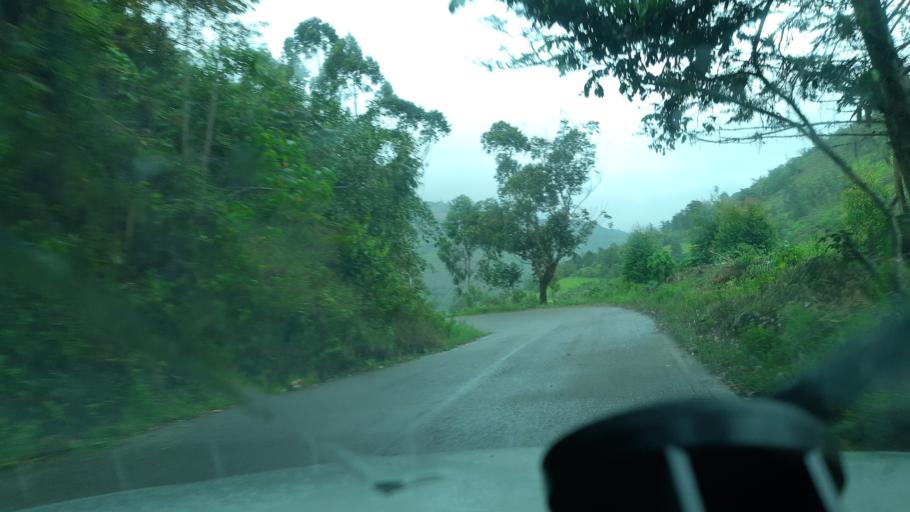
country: CO
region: Boyaca
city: Chinavita
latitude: 5.1965
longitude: -73.3819
